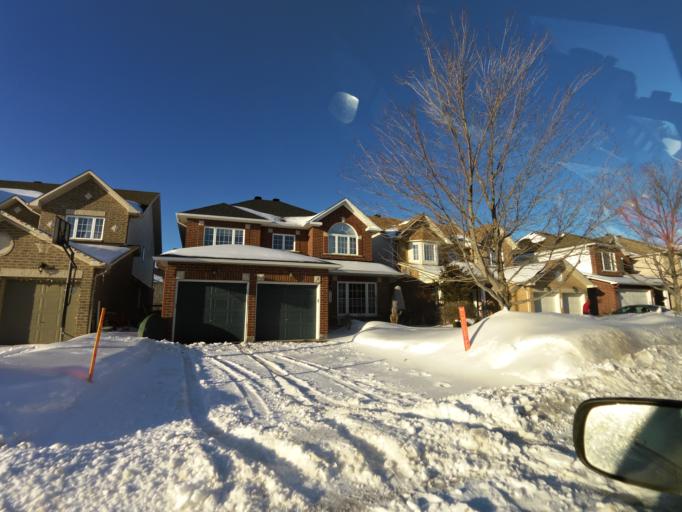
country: CA
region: Ontario
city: Ottawa
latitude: 45.4340
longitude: -75.5260
